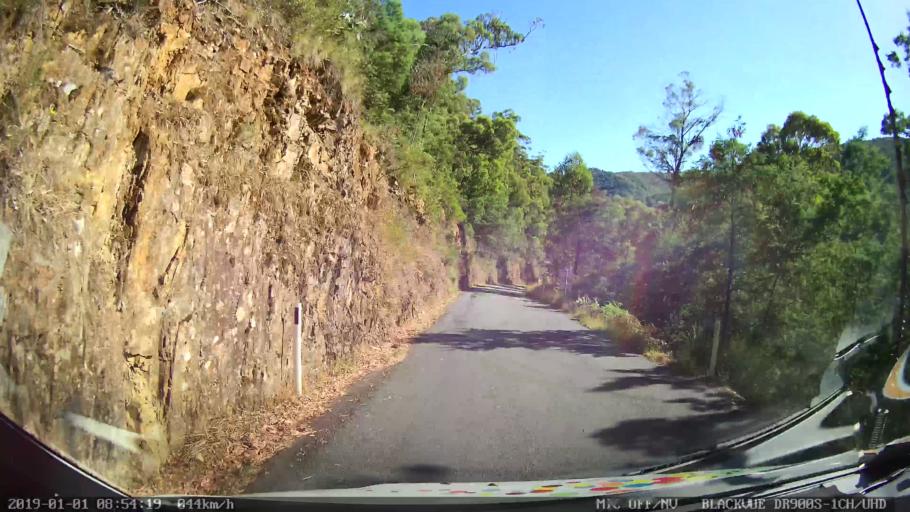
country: AU
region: New South Wales
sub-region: Snowy River
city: Jindabyne
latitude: -36.2607
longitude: 148.1909
